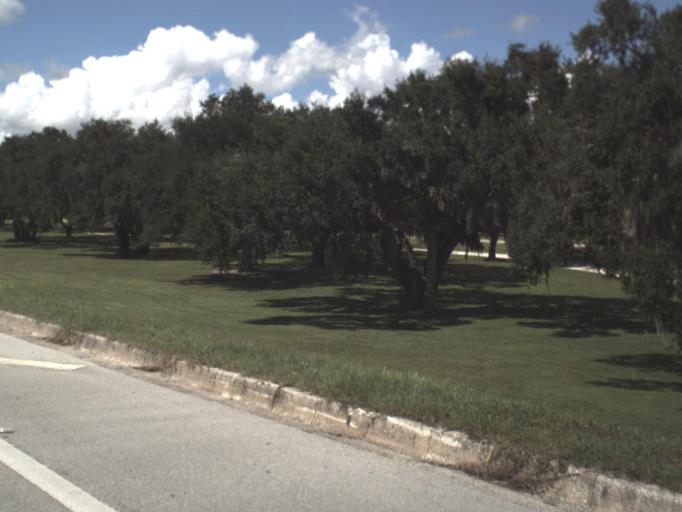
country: US
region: Florida
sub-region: DeSoto County
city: Arcadia
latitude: 27.2214
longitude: -81.8773
